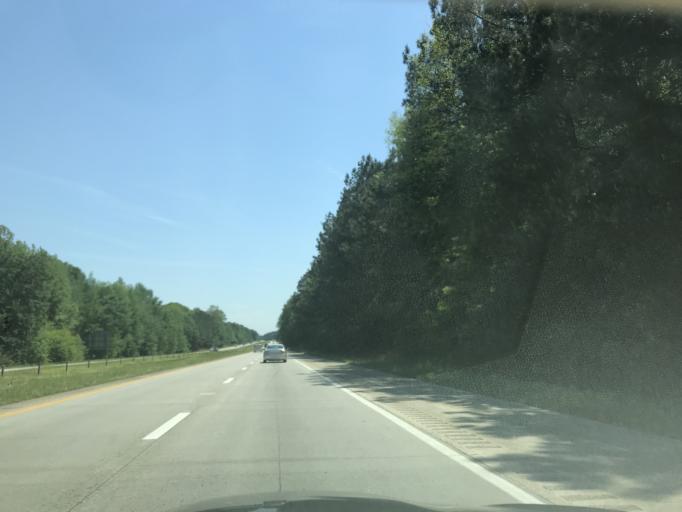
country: US
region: North Carolina
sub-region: Johnston County
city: Benson
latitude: 35.4860
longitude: -78.5518
